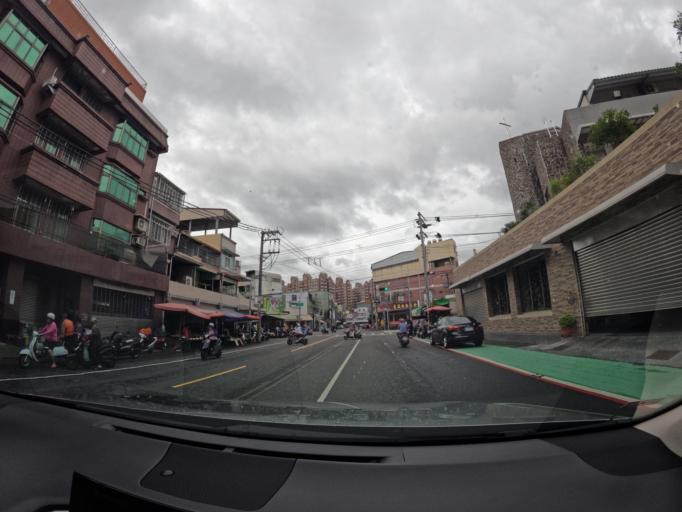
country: TW
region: Taiwan
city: Fengshan
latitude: 22.6273
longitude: 120.3738
